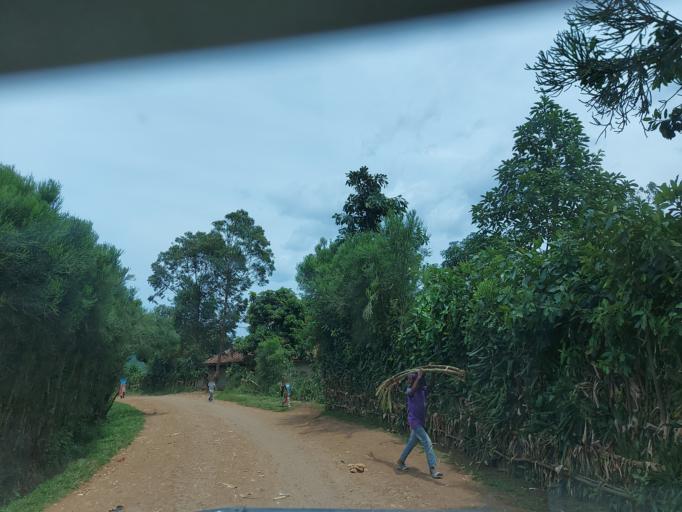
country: CD
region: South Kivu
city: Bukavu
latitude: -2.2379
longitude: 28.8435
